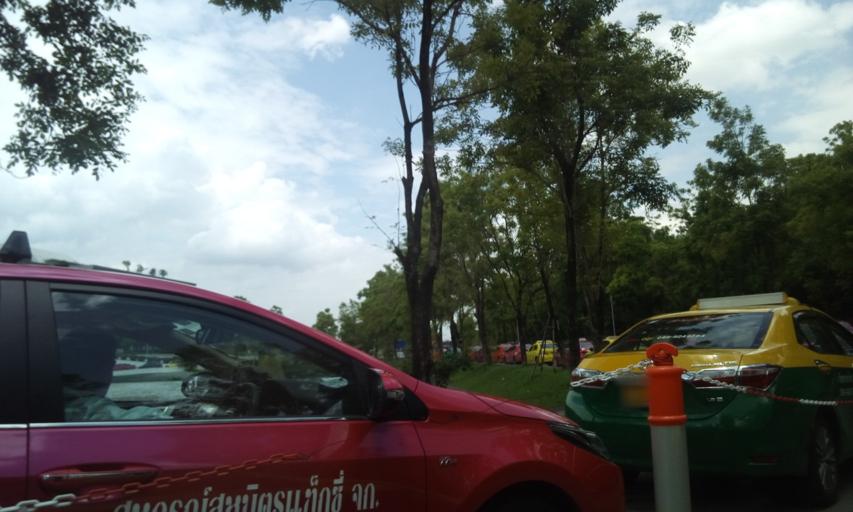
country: TH
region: Bangkok
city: Lak Si
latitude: 13.8791
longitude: 100.5625
